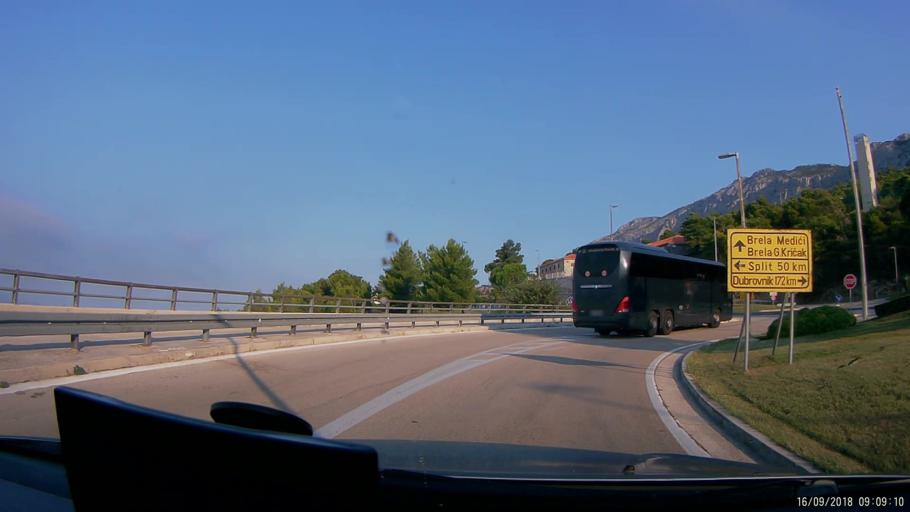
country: HR
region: Splitsko-Dalmatinska
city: Donja Brela
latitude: 43.3746
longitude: 16.9257
